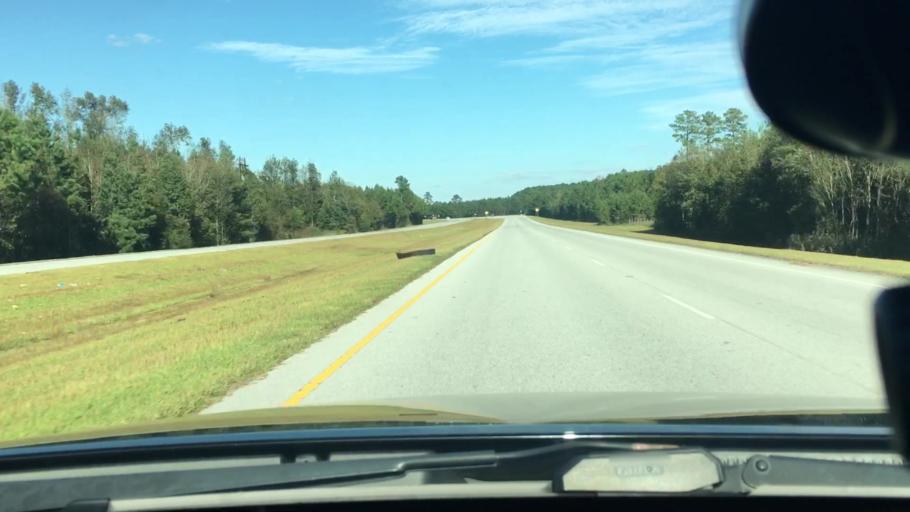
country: US
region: North Carolina
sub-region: Craven County
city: Trent Woods
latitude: 35.1380
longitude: -77.1145
